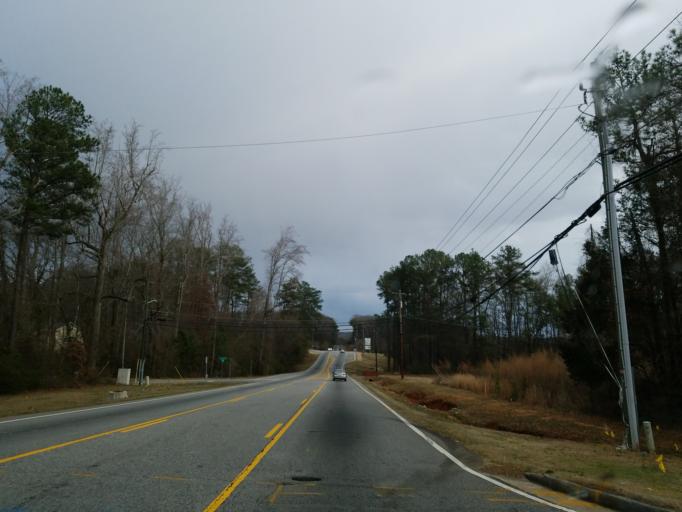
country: US
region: Georgia
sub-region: Henry County
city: Stockbridge
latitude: 33.5768
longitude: -84.2699
